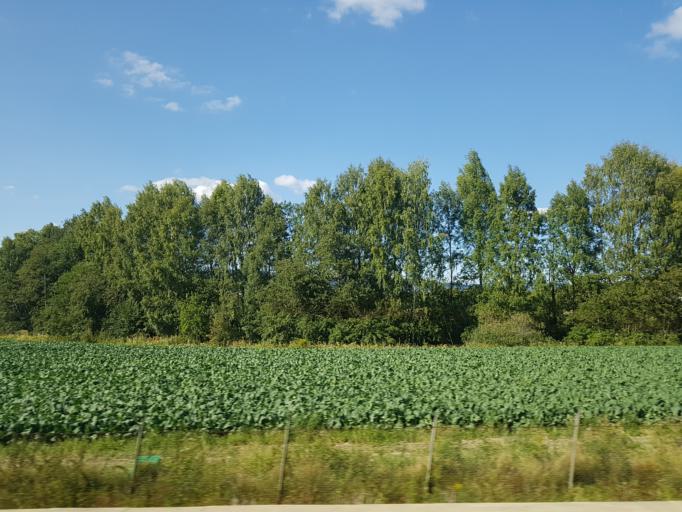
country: NO
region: Buskerud
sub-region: Lier
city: Lierbyen
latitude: 59.7598
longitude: 10.2783
